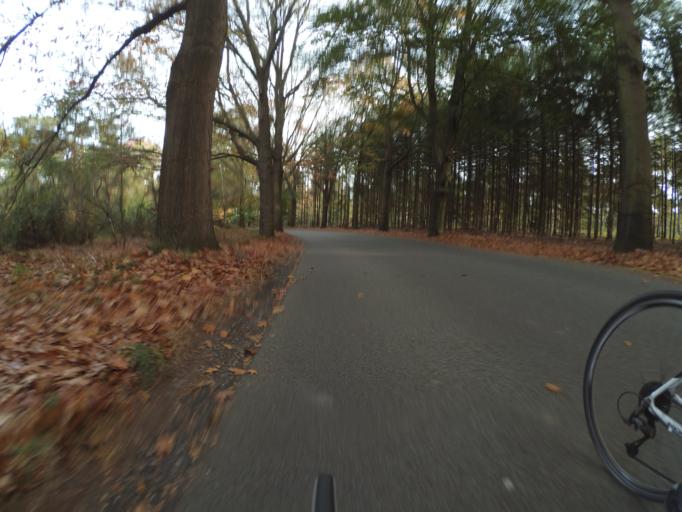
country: NL
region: Overijssel
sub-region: Gemeente Hof van Twente
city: Markelo
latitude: 52.3356
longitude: 6.4245
